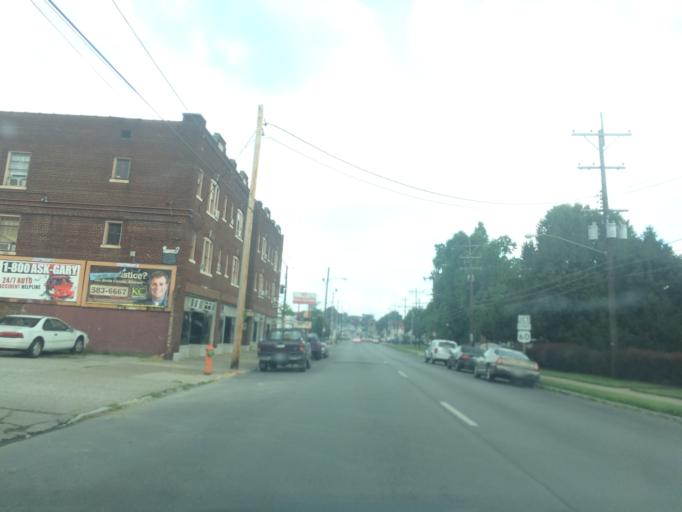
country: US
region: Kentucky
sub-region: Jefferson County
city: Audubon Park
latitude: 38.2160
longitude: -85.7444
